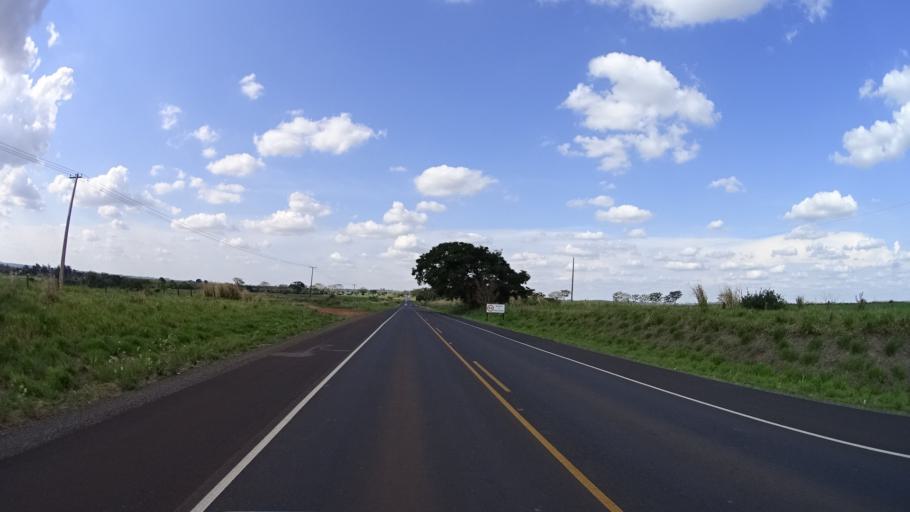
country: BR
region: Sao Paulo
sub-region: Urupes
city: Urupes
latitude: -21.0288
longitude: -49.2364
